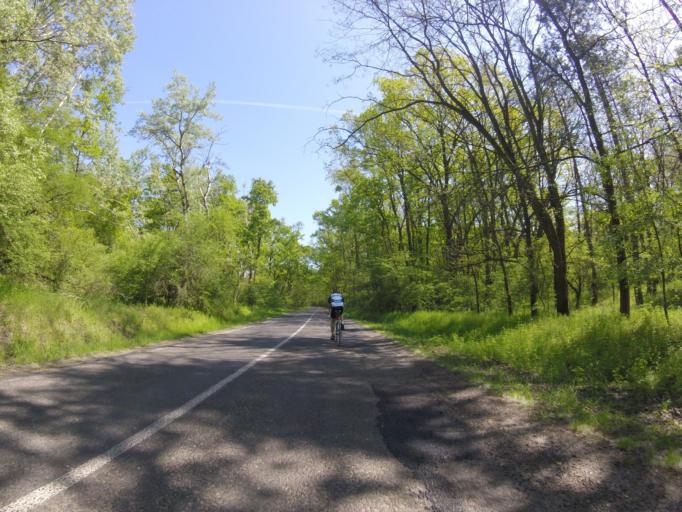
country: HU
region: Pest
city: Hernad
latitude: 47.1575
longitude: 19.4792
